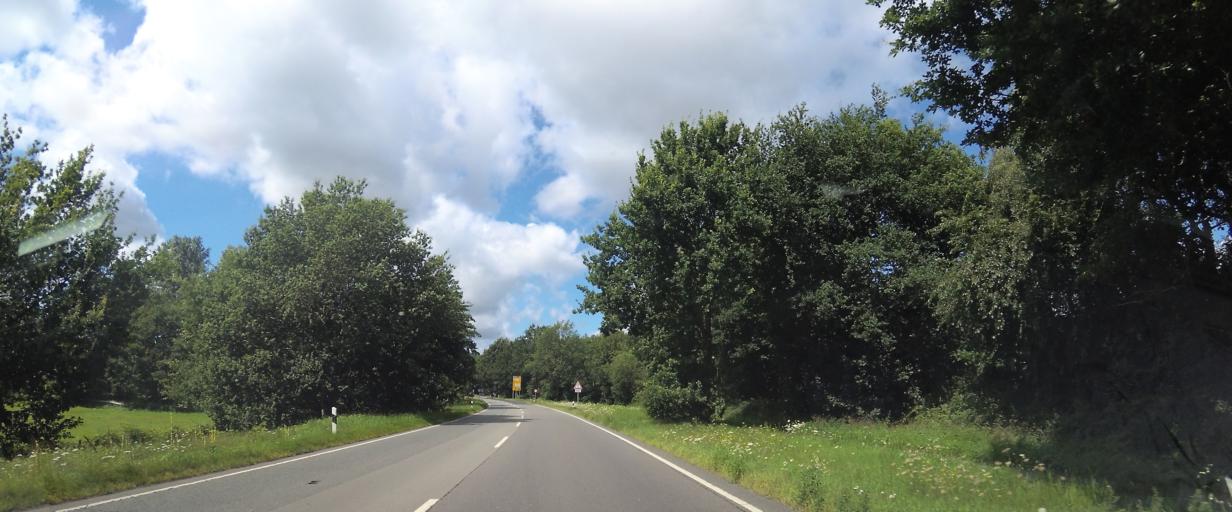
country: DE
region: Lower Saxony
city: Haren
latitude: 52.7890
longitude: 7.2700
